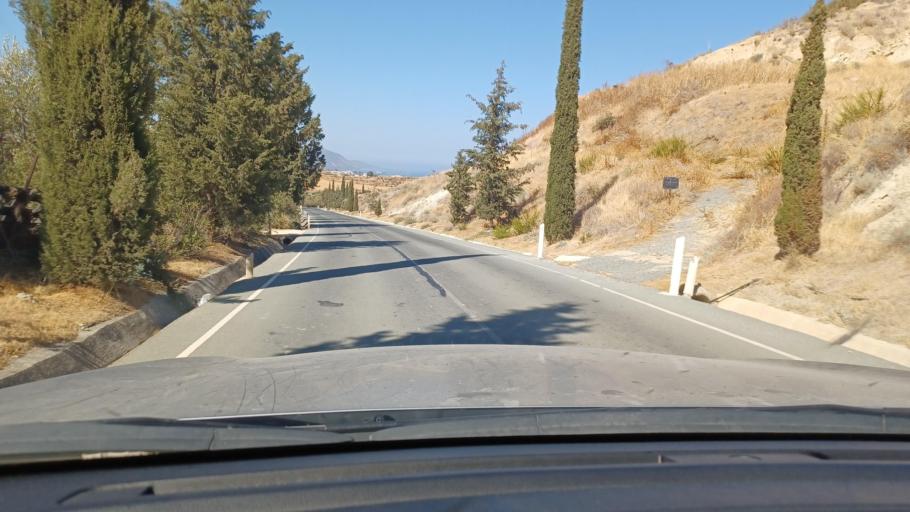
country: CY
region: Pafos
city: Polis
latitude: 35.0092
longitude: 32.4570
